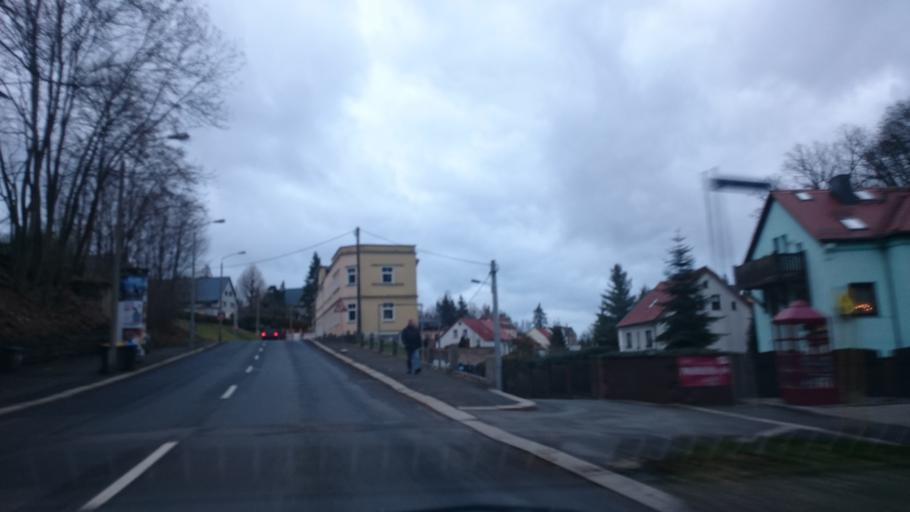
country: DE
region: Saxony
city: Lichtentanne
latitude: 50.6869
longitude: 12.4702
